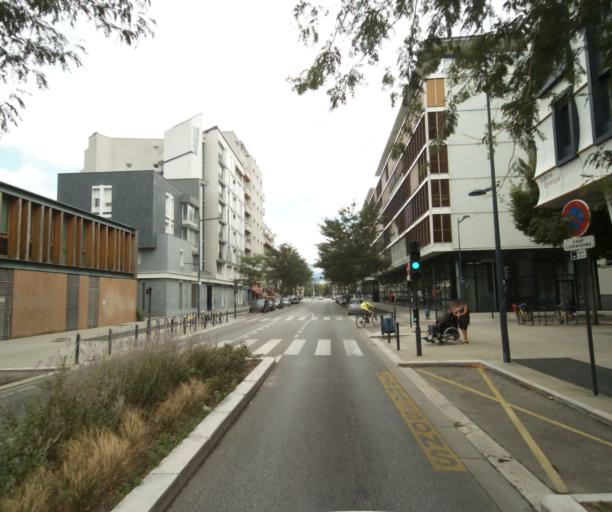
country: FR
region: Rhone-Alpes
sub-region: Departement de l'Isere
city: Grenoble
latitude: 45.1836
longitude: 5.7263
